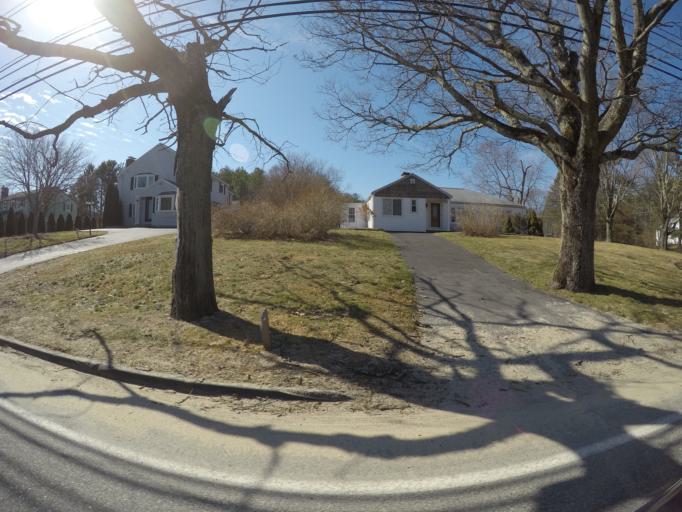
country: US
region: Massachusetts
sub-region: Norfolk County
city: Stoughton
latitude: 42.1122
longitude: -71.1346
